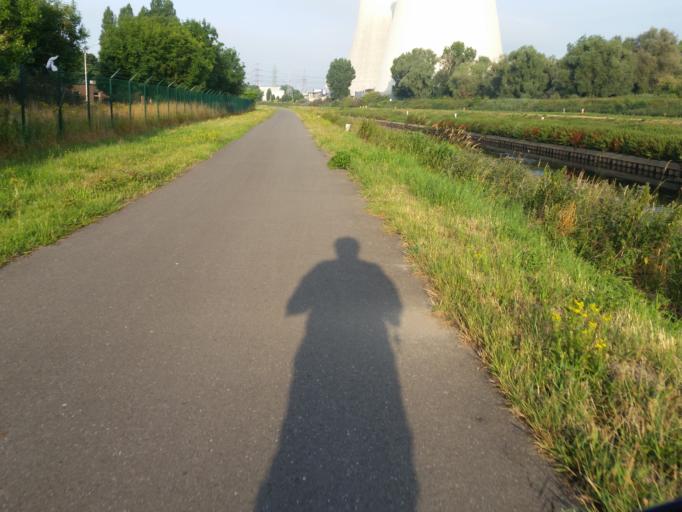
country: BE
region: Flanders
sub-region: Provincie Vlaams-Brabant
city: Vilvoorde
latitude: 50.9423
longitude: 4.4333
